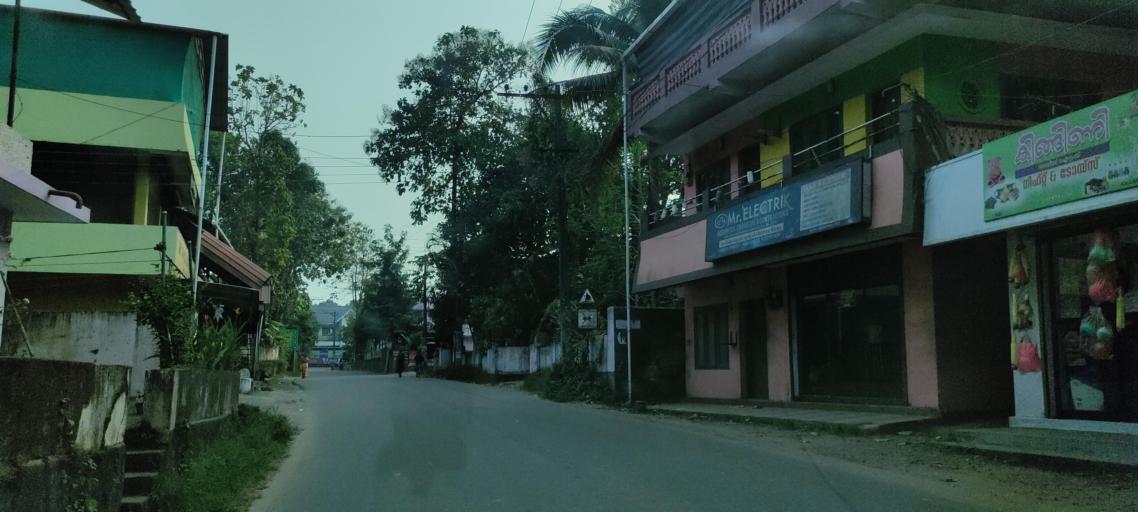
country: IN
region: Kerala
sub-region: Kottayam
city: Vaikam
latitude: 9.7001
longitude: 76.4774
